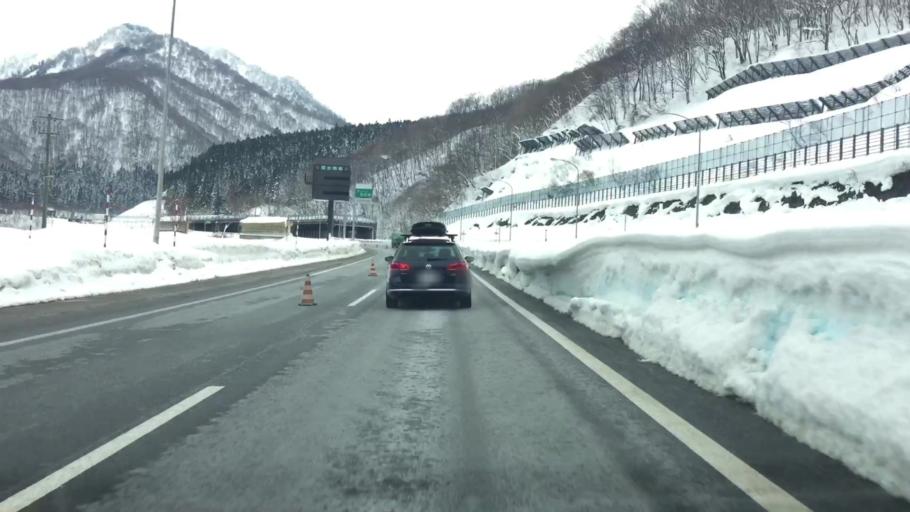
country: JP
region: Niigata
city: Shiozawa
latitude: 36.8700
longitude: 138.8659
